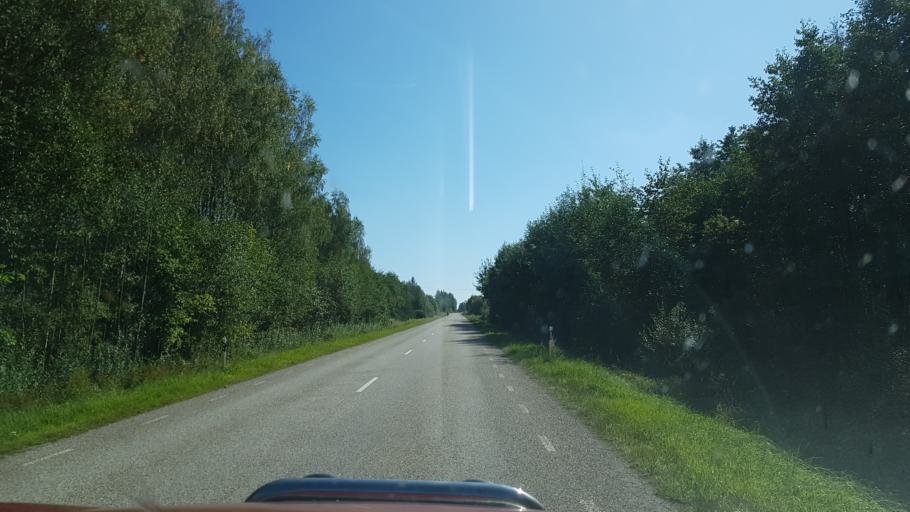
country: EE
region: Polvamaa
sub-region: Polva linn
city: Polva
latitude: 58.2451
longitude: 27.1967
